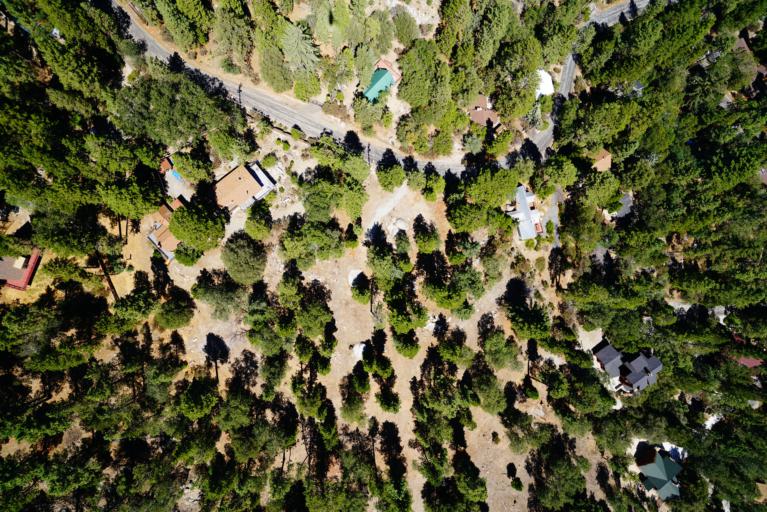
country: US
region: California
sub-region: Riverside County
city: Idyllwild-Pine Cove
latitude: 33.7514
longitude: -116.7382
